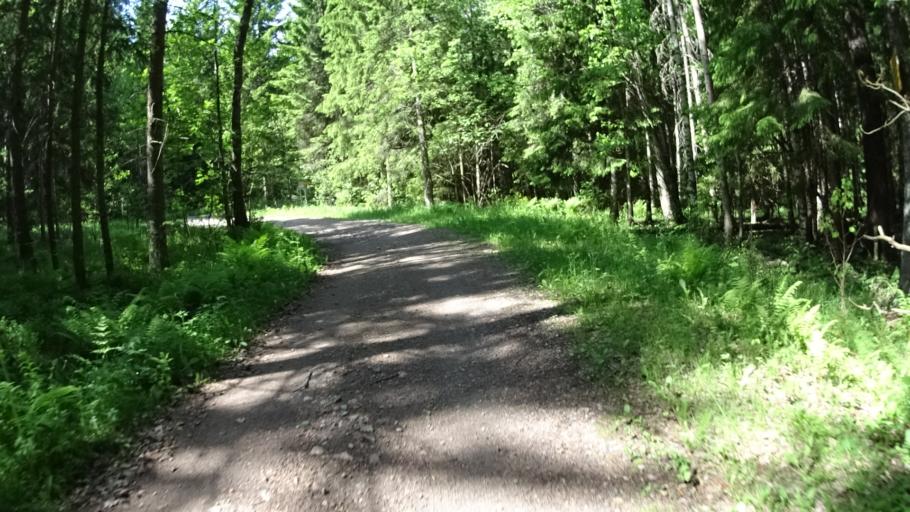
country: FI
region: Uusimaa
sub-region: Helsinki
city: Kilo
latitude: 60.3235
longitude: 24.7512
